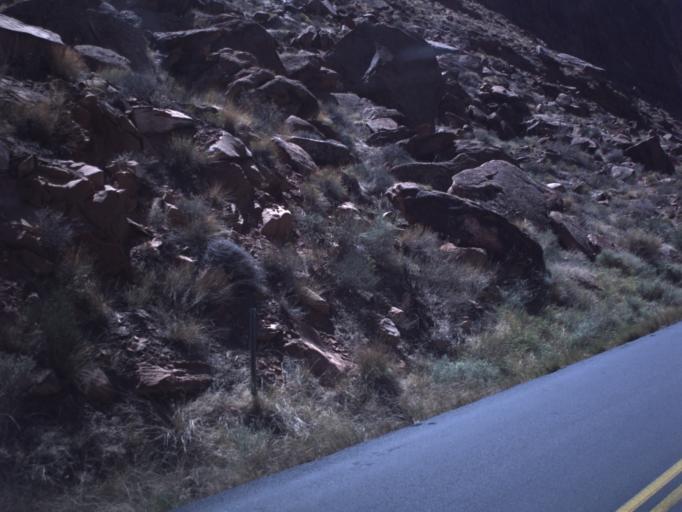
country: US
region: Utah
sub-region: Grand County
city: Moab
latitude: 38.6261
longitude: -109.5089
